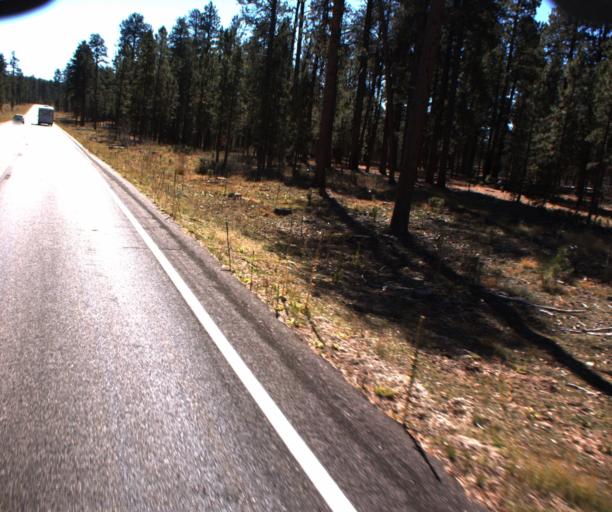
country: US
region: Arizona
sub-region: Coconino County
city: Fredonia
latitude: 36.6570
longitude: -112.1885
